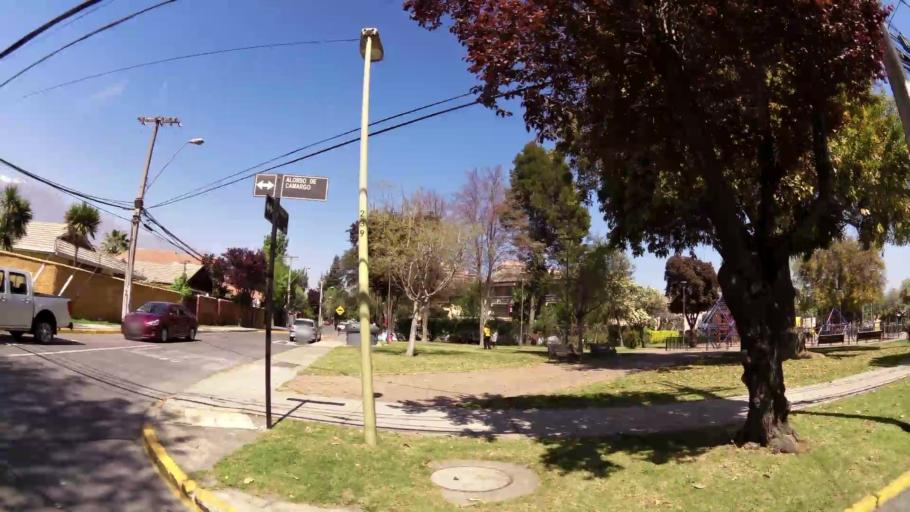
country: CL
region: Santiago Metropolitan
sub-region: Provincia de Santiago
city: Villa Presidente Frei, Nunoa, Santiago, Chile
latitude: -33.4224
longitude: -70.5525
